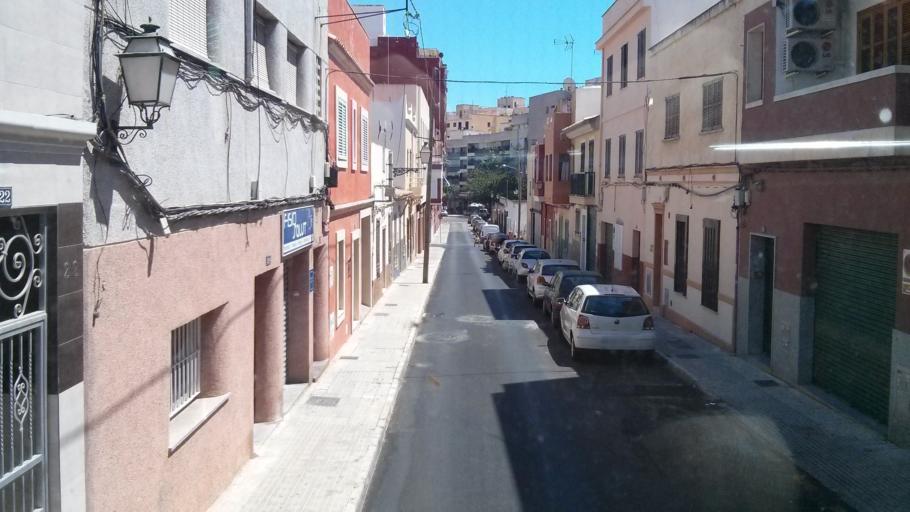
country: ES
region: Balearic Islands
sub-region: Illes Balears
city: Palma
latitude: 39.5725
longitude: 2.6296
